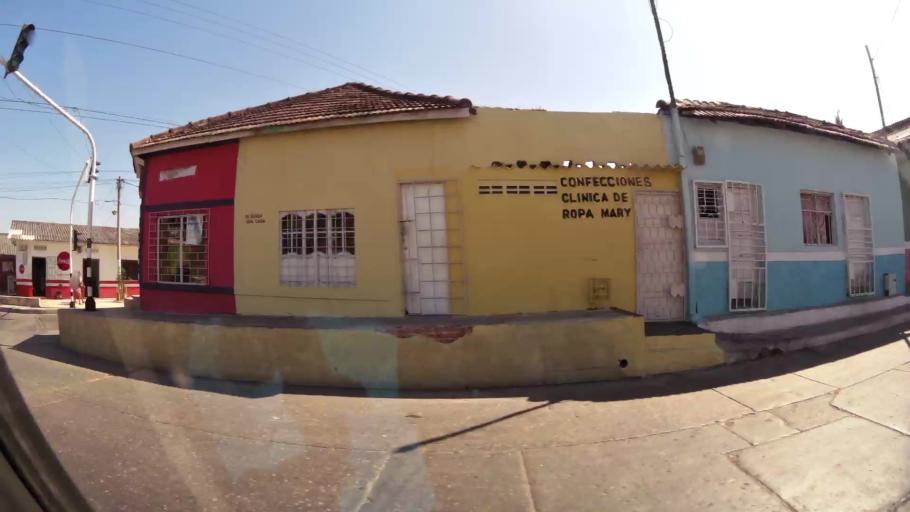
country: CO
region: Atlantico
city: Barranquilla
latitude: 10.9704
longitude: -74.7845
